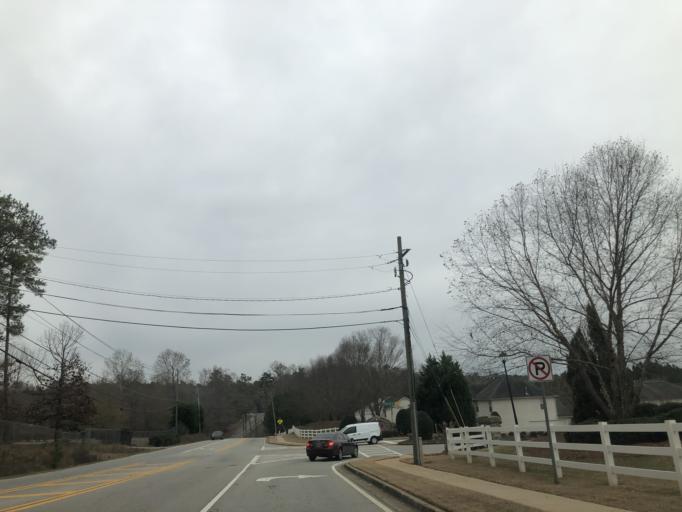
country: US
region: Georgia
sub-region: Henry County
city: Stockbridge
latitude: 33.6046
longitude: -84.2651
